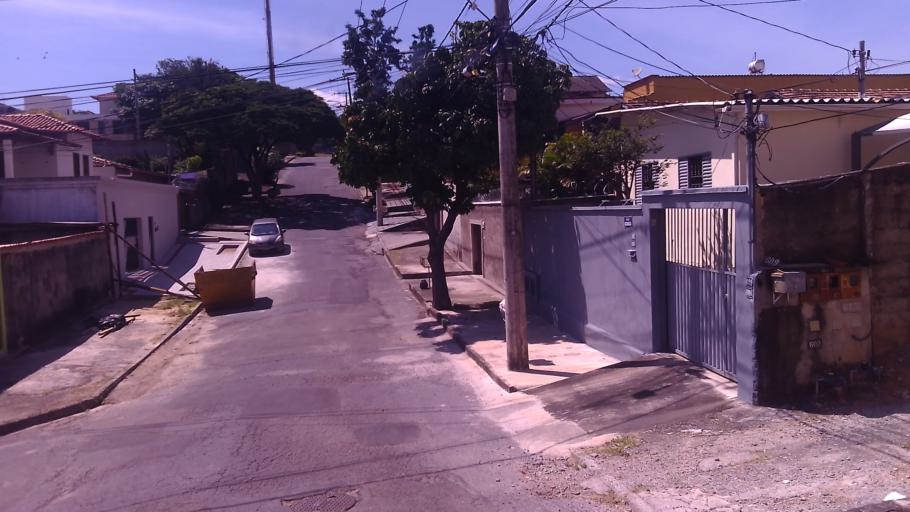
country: BR
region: Minas Gerais
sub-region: Contagem
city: Contagem
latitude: -19.9145
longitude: -44.0013
